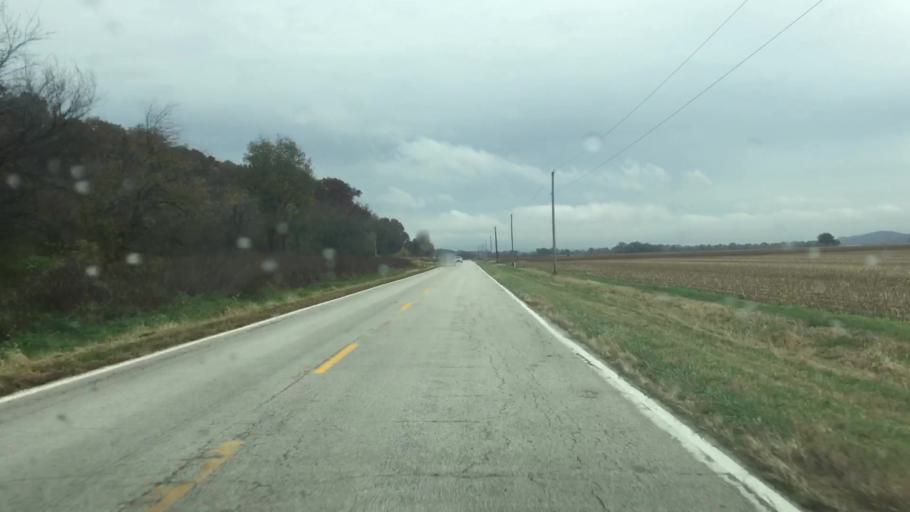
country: US
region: Missouri
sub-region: Gasconade County
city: Hermann
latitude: 38.7070
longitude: -91.5492
